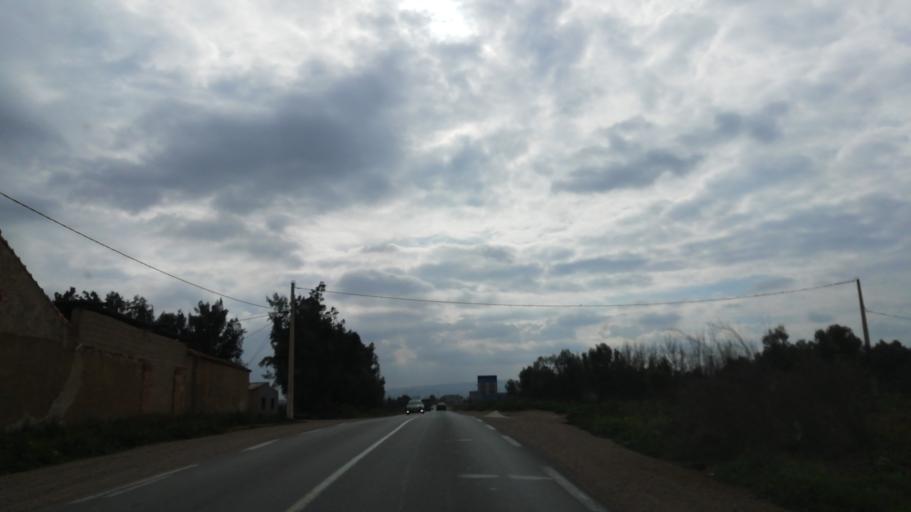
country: DZ
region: Oran
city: Sidi ech Chahmi
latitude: 35.5717
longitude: -0.4507
